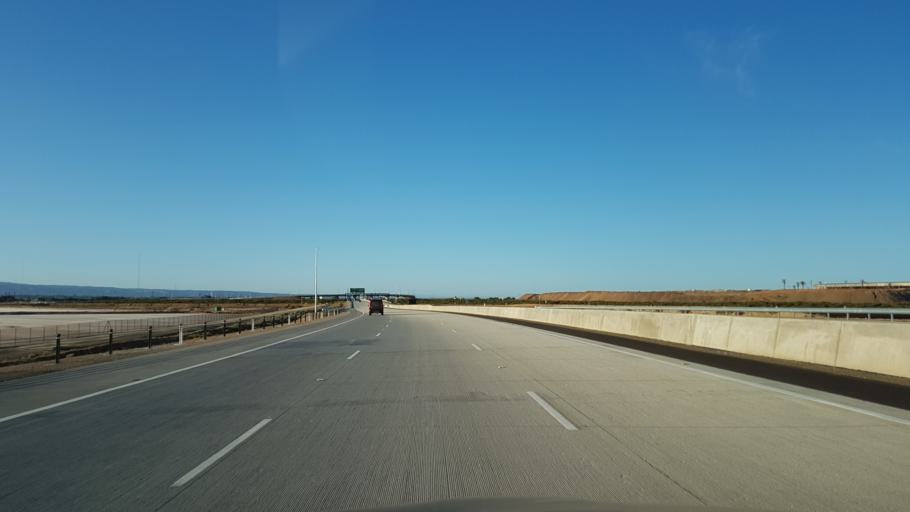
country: AU
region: South Australia
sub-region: Port Adelaide Enfield
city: Enfield
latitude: -34.8176
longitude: 138.5618
